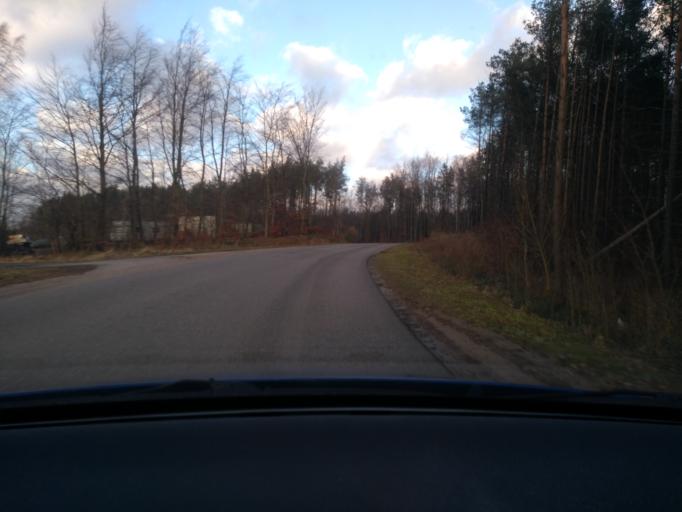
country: PL
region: Pomeranian Voivodeship
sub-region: Powiat kartuski
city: Kartuzy
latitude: 54.3670
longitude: 18.2179
